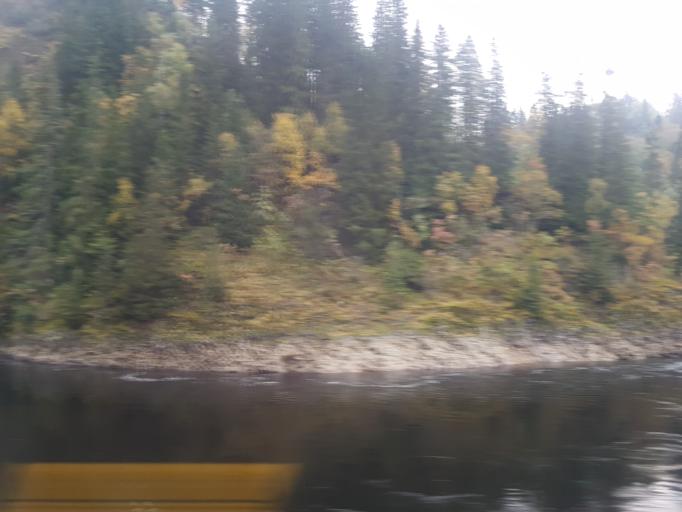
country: NO
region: Sor-Trondelag
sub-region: Midtre Gauldal
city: Storen
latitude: 63.0550
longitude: 10.2885
